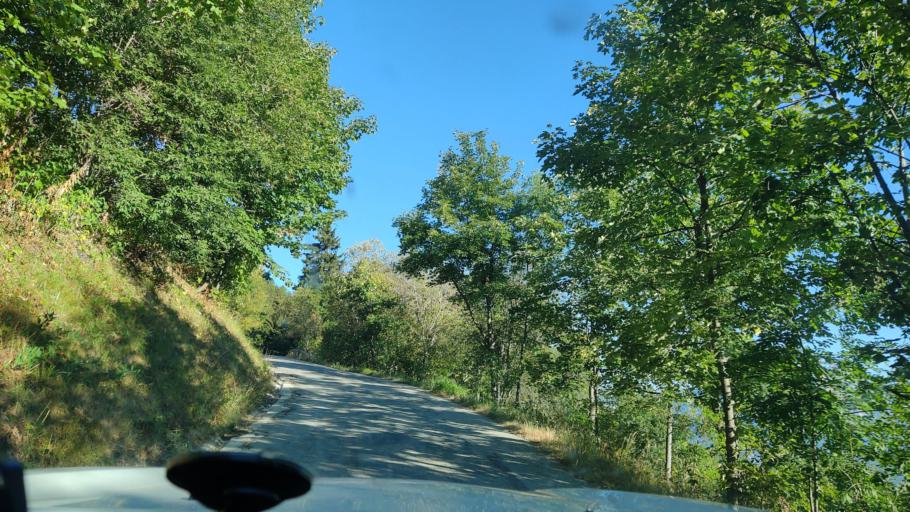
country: FR
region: Rhone-Alpes
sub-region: Departement de la Savoie
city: Saint-Michel-de-Maurienne
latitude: 45.1844
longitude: 6.4724
